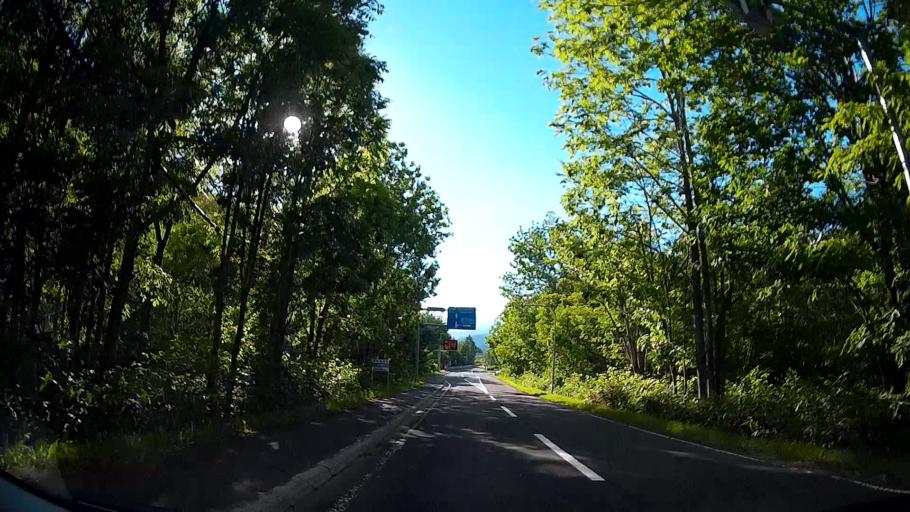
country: JP
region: Hokkaido
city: Sapporo
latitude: 42.9754
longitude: 141.1401
